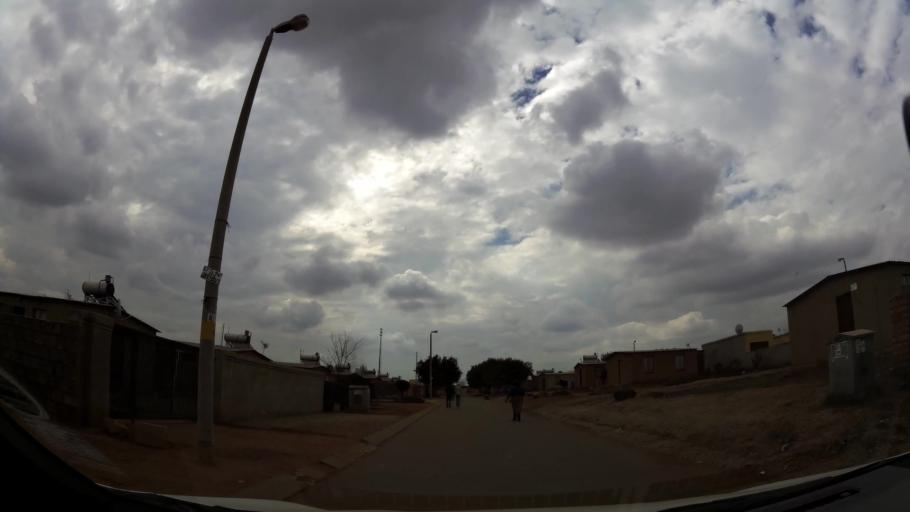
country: ZA
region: Gauteng
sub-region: Ekurhuleni Metropolitan Municipality
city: Germiston
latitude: -26.3721
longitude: 28.1192
